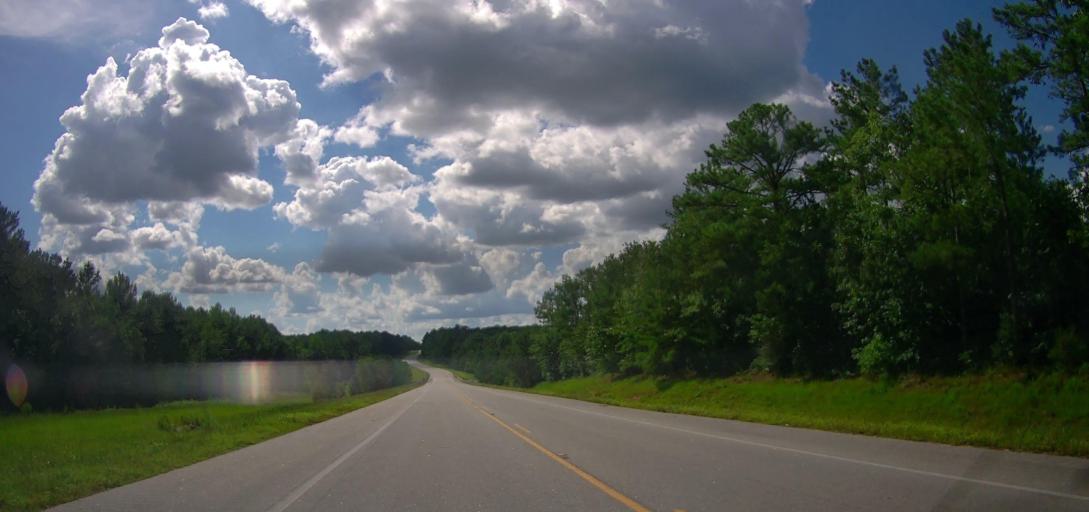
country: US
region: Alabama
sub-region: Lee County
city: Auburn
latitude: 32.4389
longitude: -85.4874
